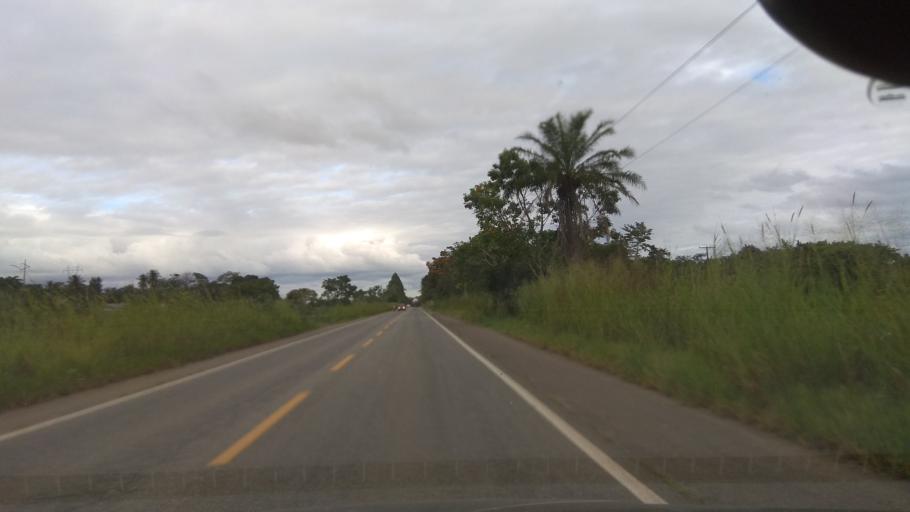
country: BR
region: Bahia
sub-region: Ipiau
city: Ipiau
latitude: -14.1578
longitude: -39.6945
